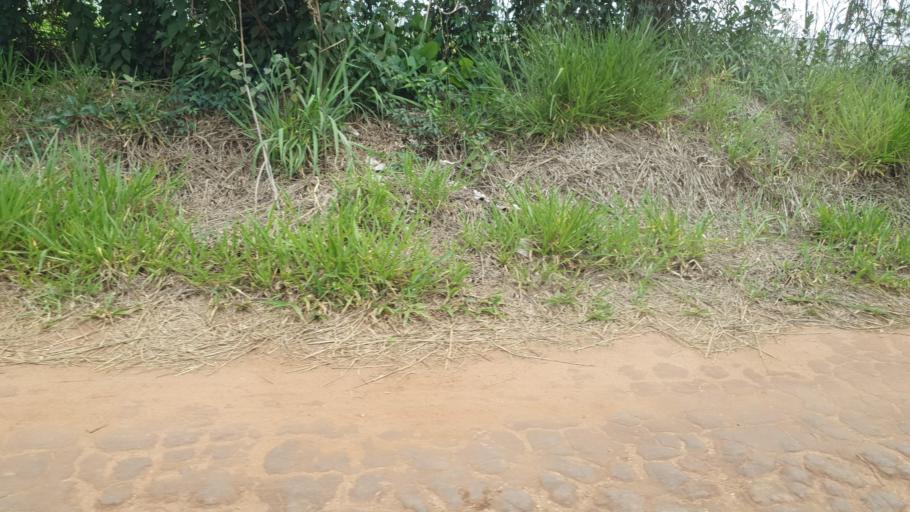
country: BR
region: Sao Paulo
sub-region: Sorocaba
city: Sorocaba
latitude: -23.4536
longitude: -47.4083
